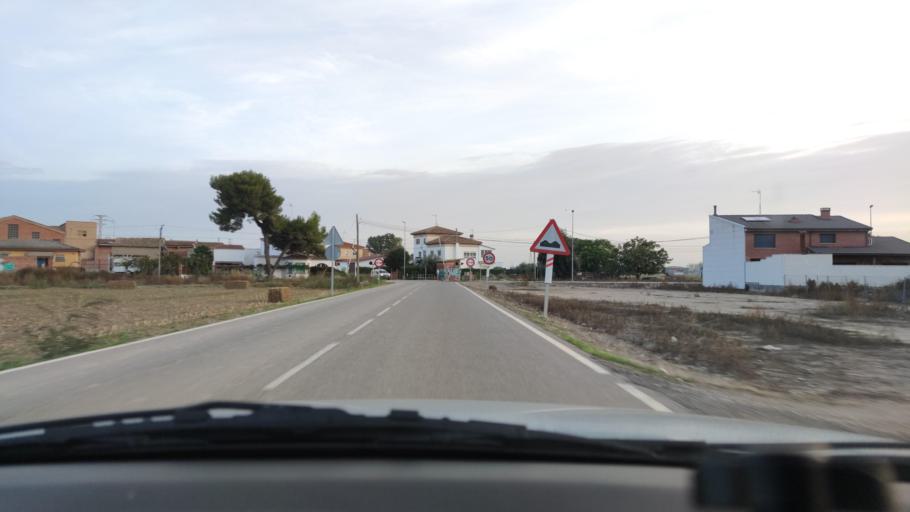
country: ES
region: Catalonia
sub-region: Provincia de Lleida
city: Mollerussa
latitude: 41.6309
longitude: 0.8764
